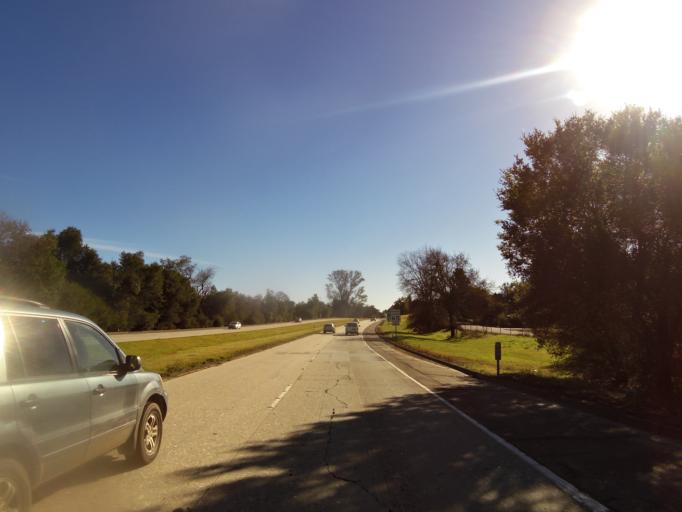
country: US
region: California
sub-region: Sonoma County
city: Cloverdale
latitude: 38.7756
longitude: -123.0023
